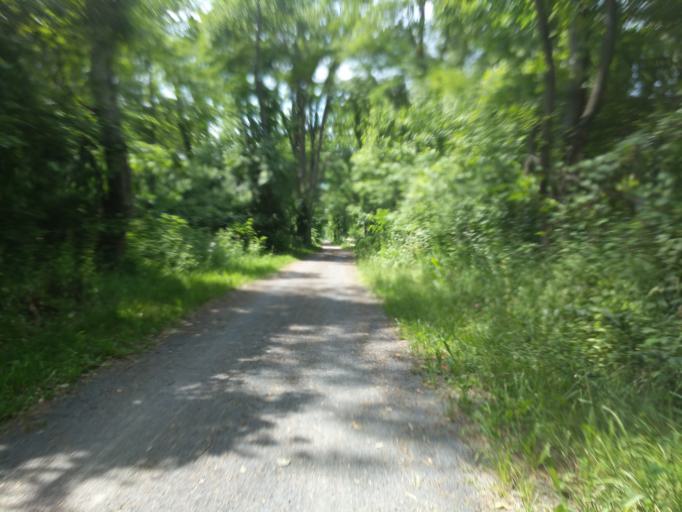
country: US
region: New York
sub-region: Tompkins County
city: Northwest Ithaca
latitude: 42.5142
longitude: -76.5641
